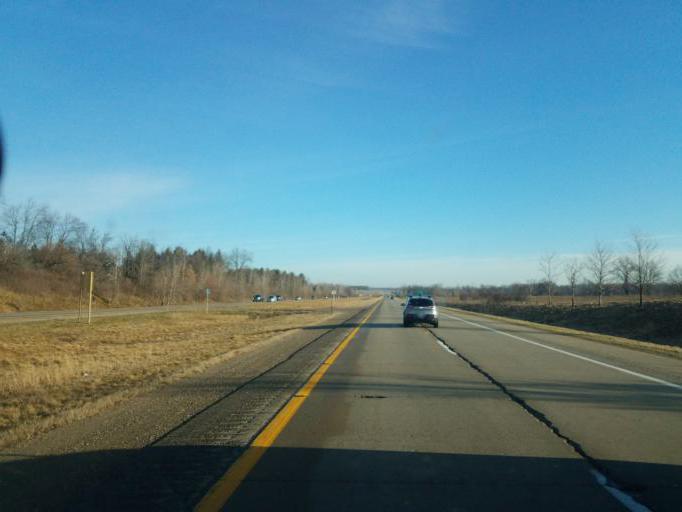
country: US
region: Michigan
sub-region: Clinton County
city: DeWitt
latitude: 42.8457
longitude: -84.5186
